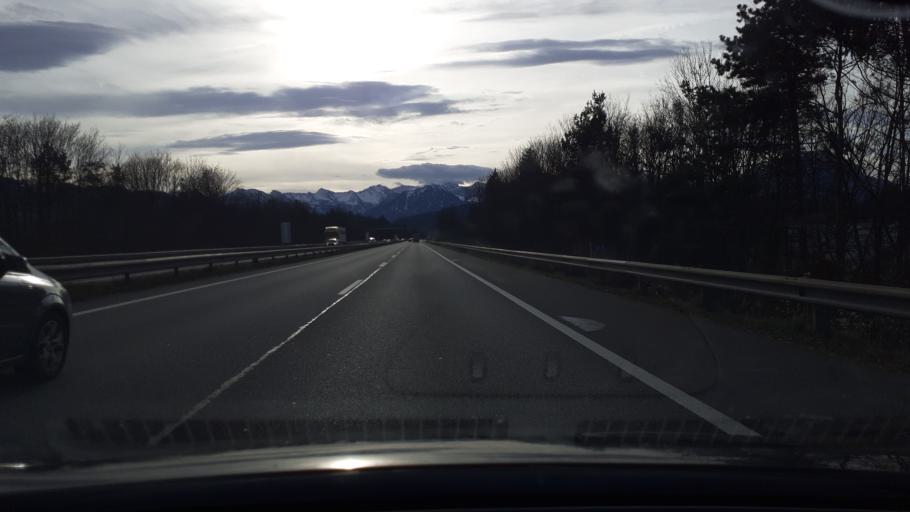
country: AT
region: Vorarlberg
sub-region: Politischer Bezirk Feldkirch
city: Klaus
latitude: 47.2997
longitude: 9.6241
